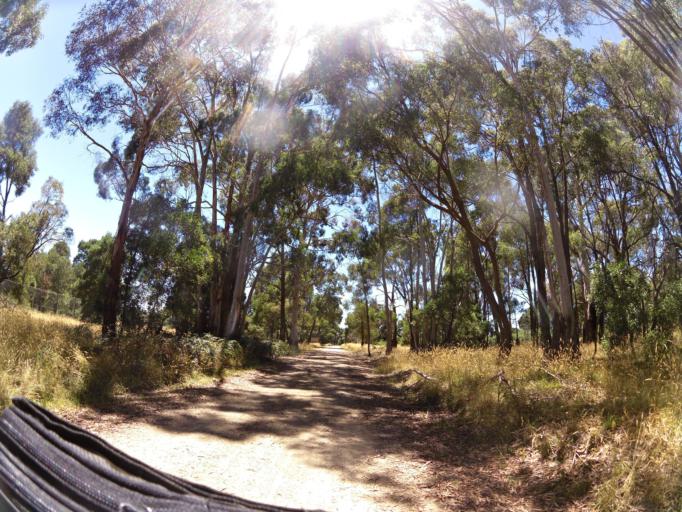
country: AU
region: Victoria
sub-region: Ballarat North
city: Delacombe
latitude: -37.6223
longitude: 143.7046
